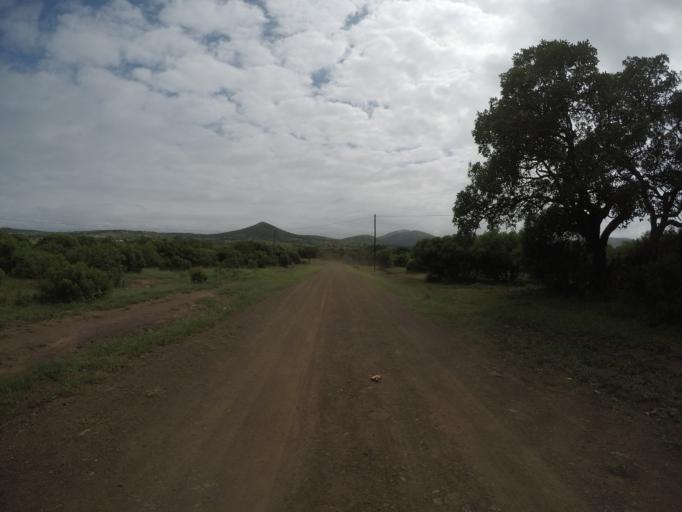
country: ZA
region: KwaZulu-Natal
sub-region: uThungulu District Municipality
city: Empangeni
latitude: -28.6226
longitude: 31.8557
